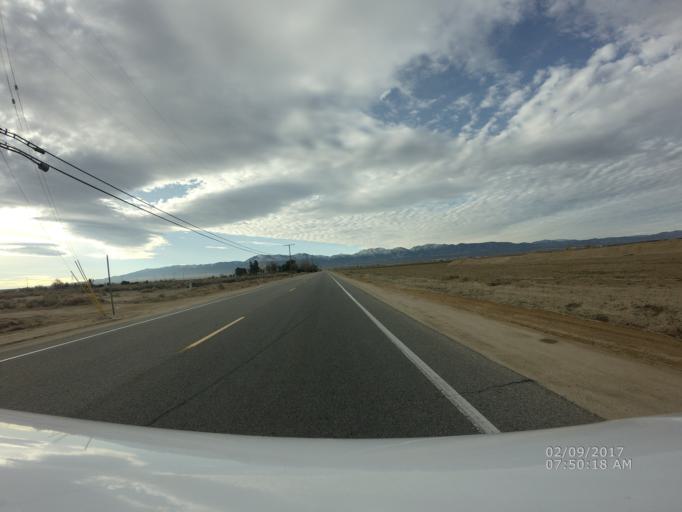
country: US
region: California
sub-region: Los Angeles County
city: Lake Los Angeles
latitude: 34.5795
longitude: -117.8268
